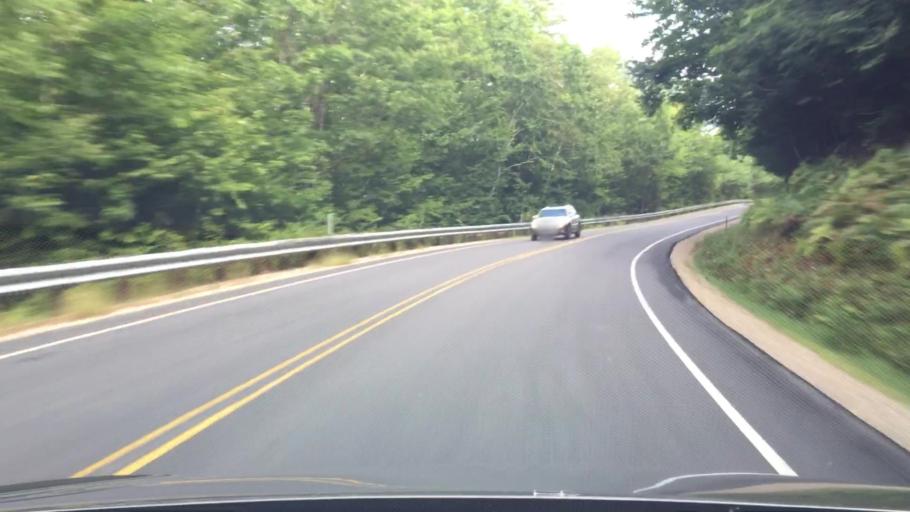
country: US
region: New Hampshire
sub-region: Carroll County
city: Conway
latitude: 43.9911
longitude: -71.1701
